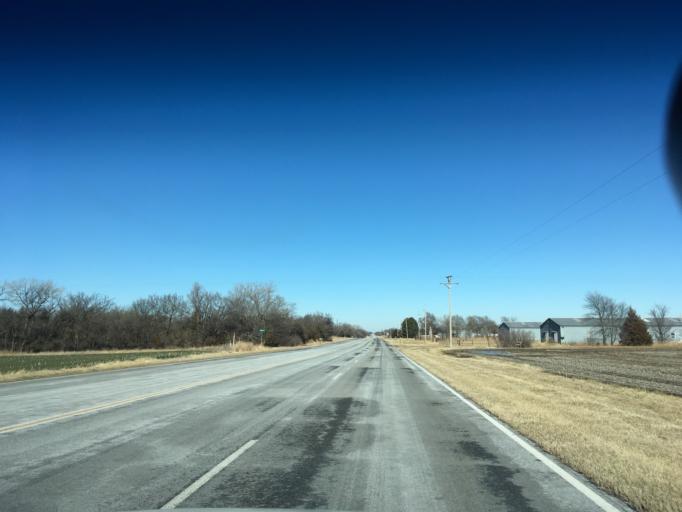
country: US
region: Kansas
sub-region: Harvey County
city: Sedgwick
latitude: 37.9256
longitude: -97.3363
